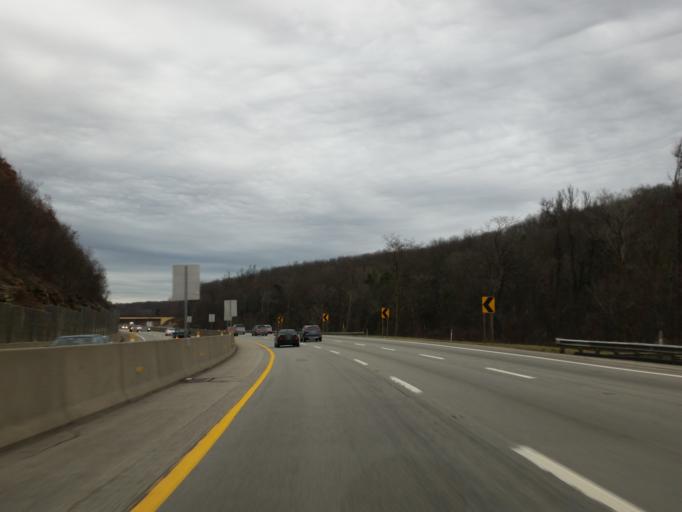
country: US
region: Pennsylvania
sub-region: Fayette County
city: Bear Rocks
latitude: 40.1496
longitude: -79.4286
